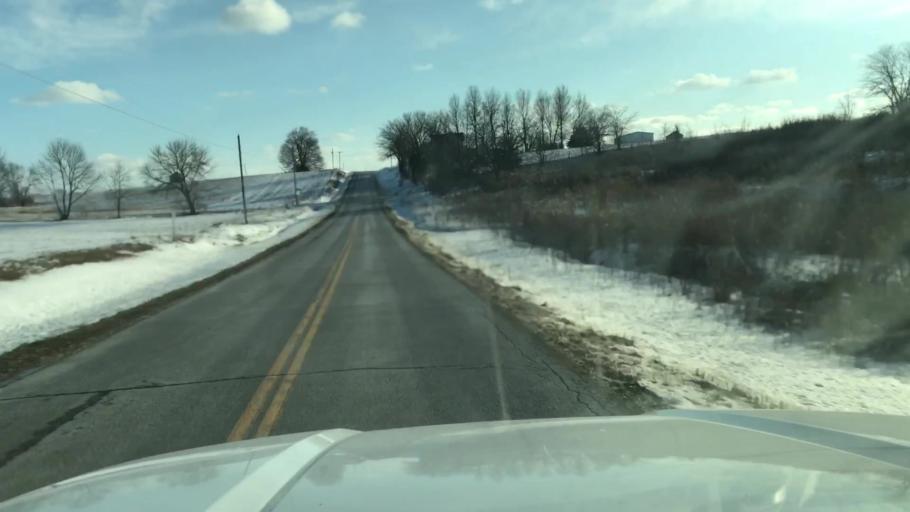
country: US
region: Missouri
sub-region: Holt County
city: Oregon
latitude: 40.0584
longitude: -94.9749
